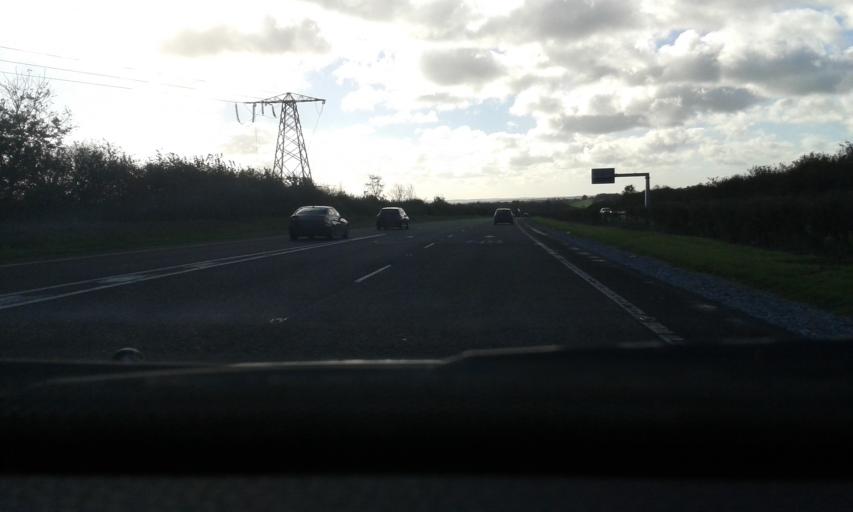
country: IE
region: Munster
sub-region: County Cork
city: Watergrasshill
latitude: 52.0044
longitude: -8.3442
